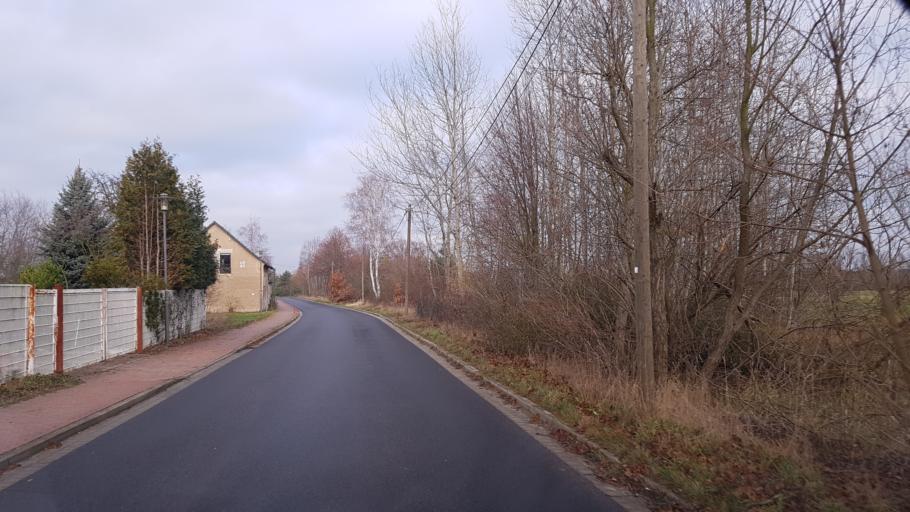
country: DE
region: Brandenburg
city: Sallgast
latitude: 51.5887
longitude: 13.8150
